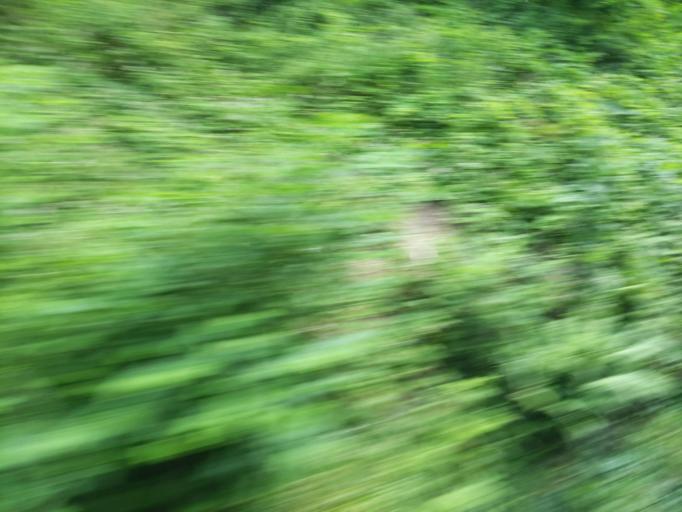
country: GB
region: England
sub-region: Cornwall
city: Par
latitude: 50.3700
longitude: -4.6829
